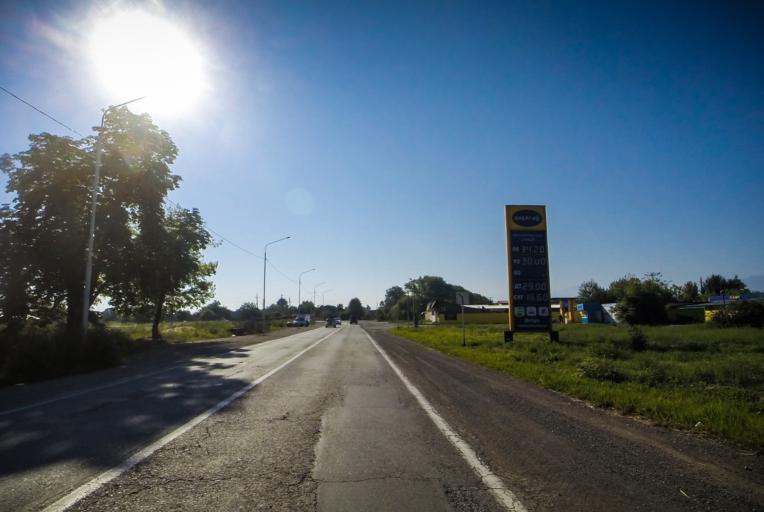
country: RU
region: North Ossetia
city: Arkhonskaya
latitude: 43.1157
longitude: 44.4932
